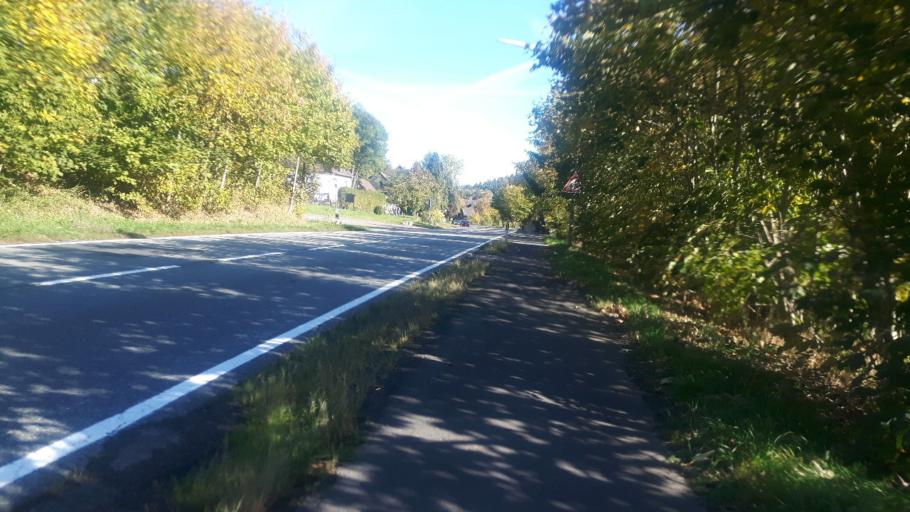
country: DE
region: Rheinland-Pfalz
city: Wissen
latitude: 50.7889
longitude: 7.7591
